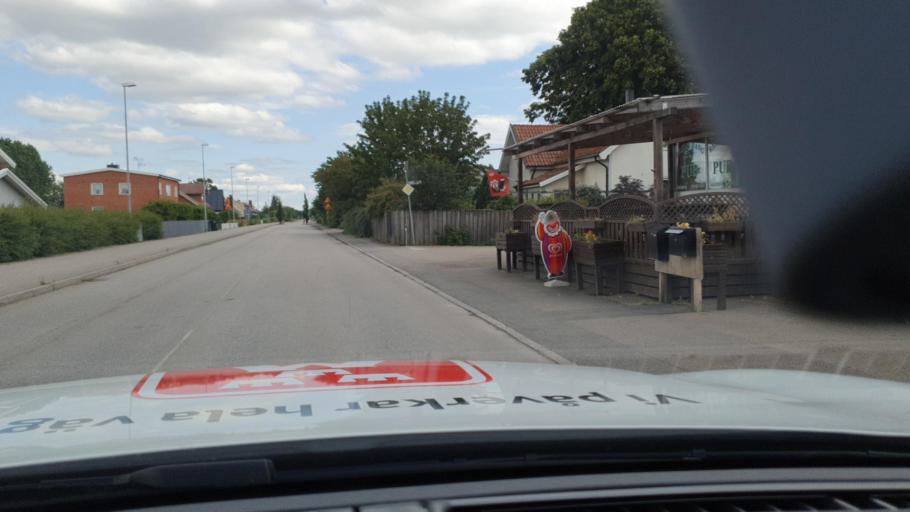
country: SE
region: Skane
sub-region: Astorps Kommun
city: Kvidinge
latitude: 56.1335
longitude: 13.0526
